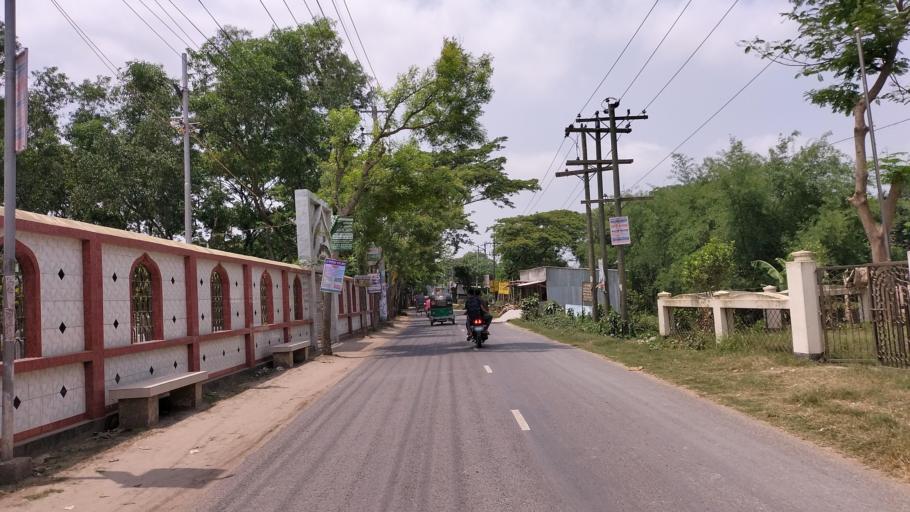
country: BD
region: Dhaka
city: Azimpur
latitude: 23.7296
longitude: 90.2827
